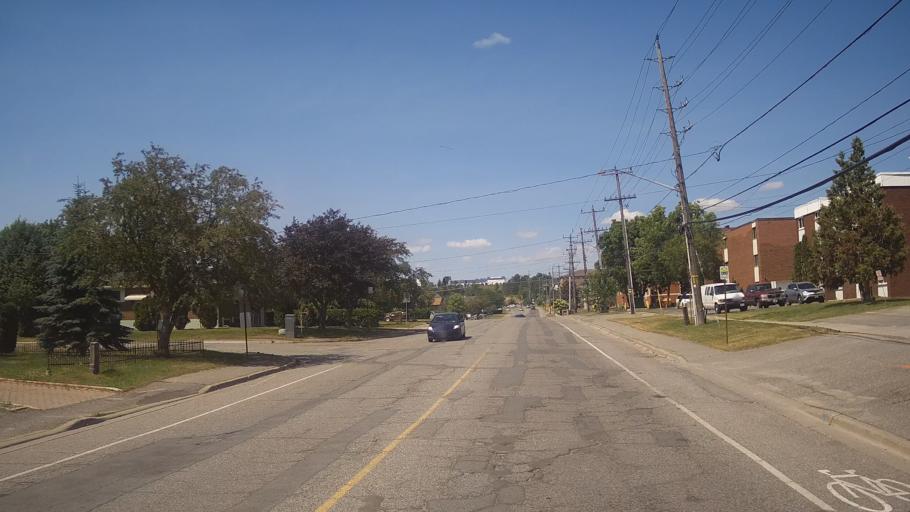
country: CA
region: Ontario
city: Greater Sudbury
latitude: 46.4604
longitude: -81.0280
